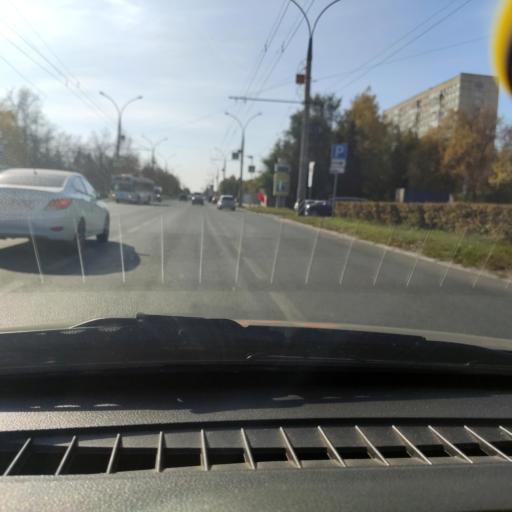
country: RU
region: Samara
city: Tol'yatti
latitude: 53.5248
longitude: 49.2751
